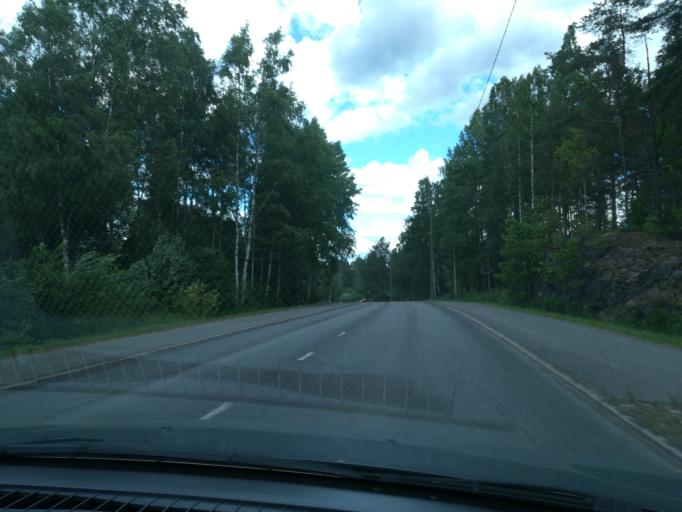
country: FI
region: Southern Savonia
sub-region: Mikkeli
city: Maentyharju
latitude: 61.4220
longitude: 26.8925
